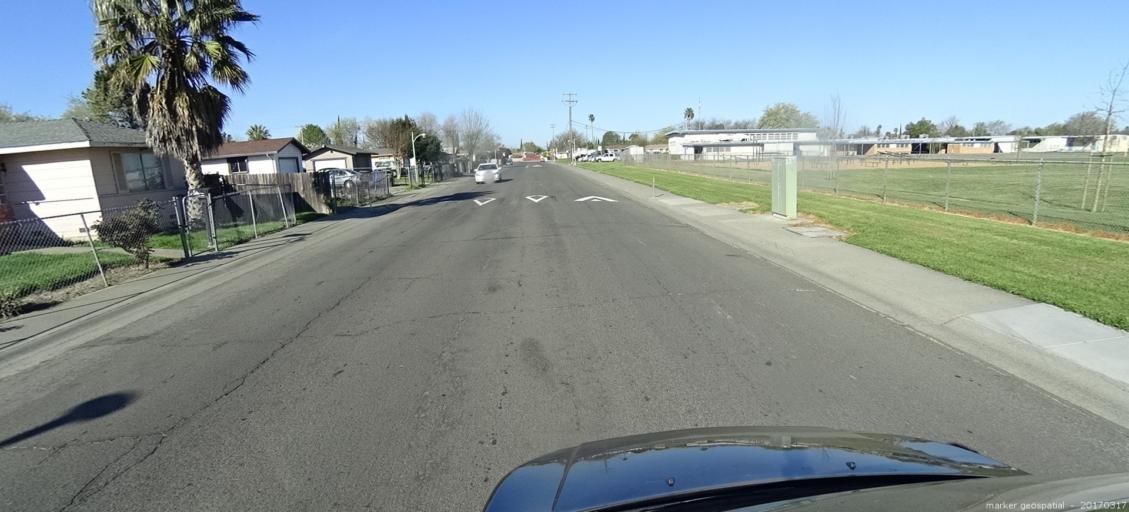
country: US
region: California
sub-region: Sacramento County
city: Parkway
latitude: 38.4863
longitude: -121.4853
